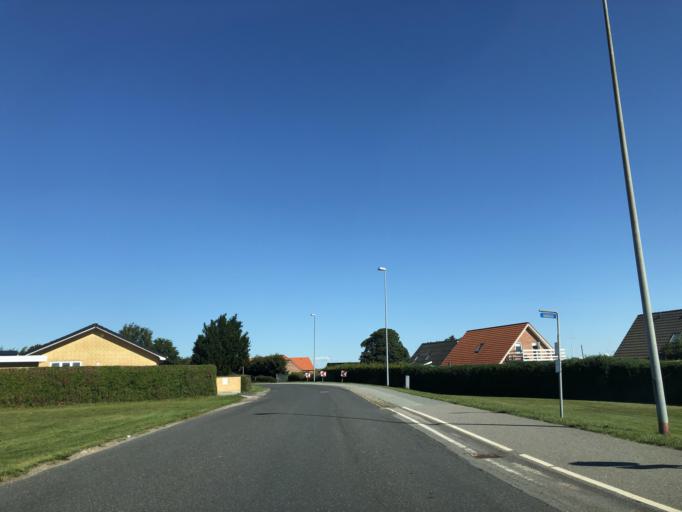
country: DK
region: North Denmark
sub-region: Mariagerfjord Kommune
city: Hobro
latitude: 56.6439
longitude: 9.7788
